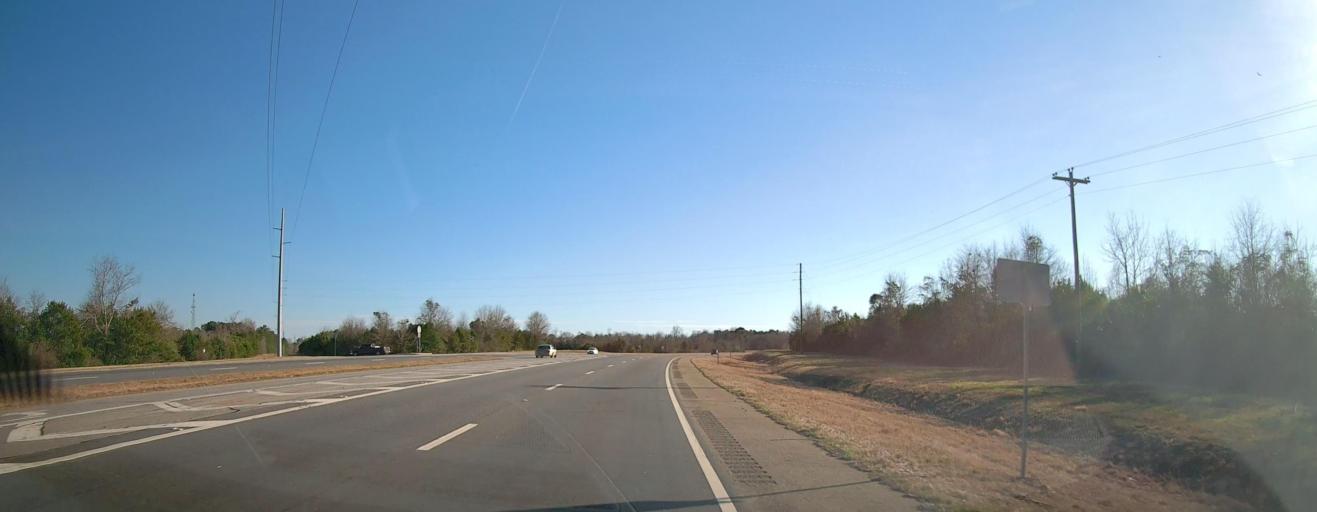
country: US
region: Georgia
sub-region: Sumter County
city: Americus
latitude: 31.9118
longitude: -84.2597
